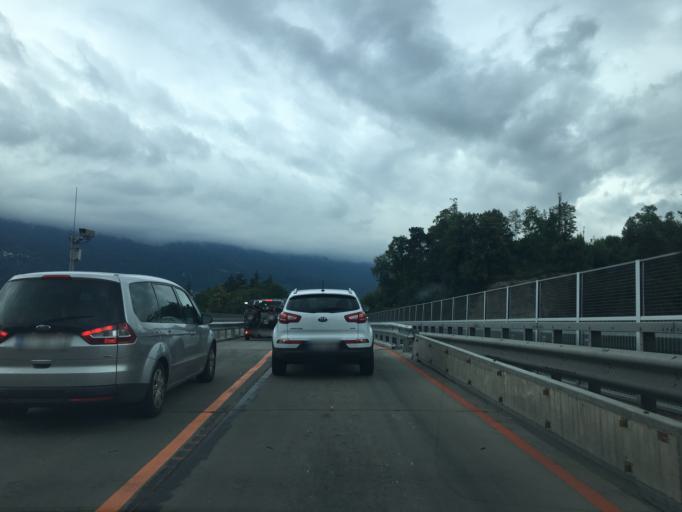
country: AT
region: Tyrol
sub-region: Innsbruck Stadt
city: Innsbruck
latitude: 47.2492
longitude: 11.4029
